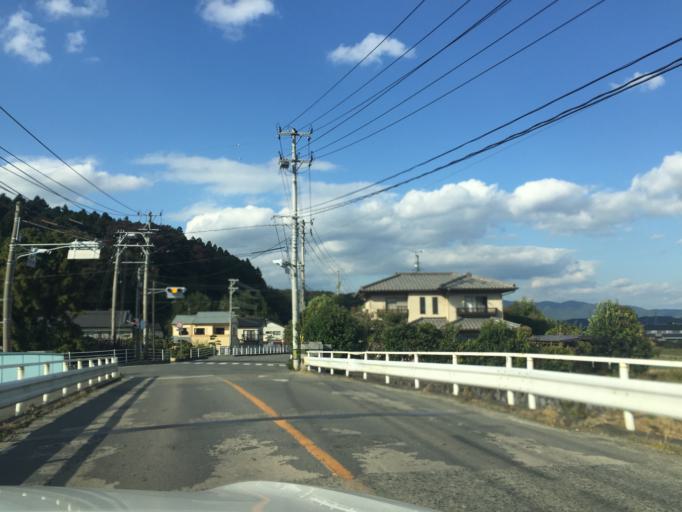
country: JP
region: Fukushima
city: Iwaki
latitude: 37.0629
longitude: 140.8703
